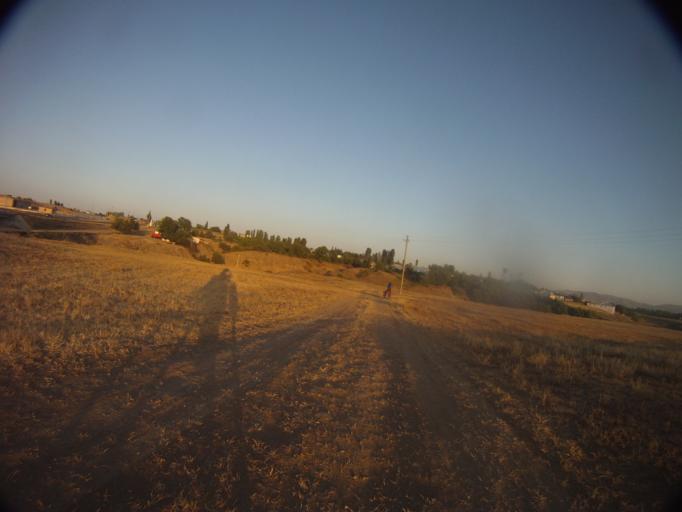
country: AZ
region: Agstafa
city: Vurgun
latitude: 41.1025
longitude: 45.5028
